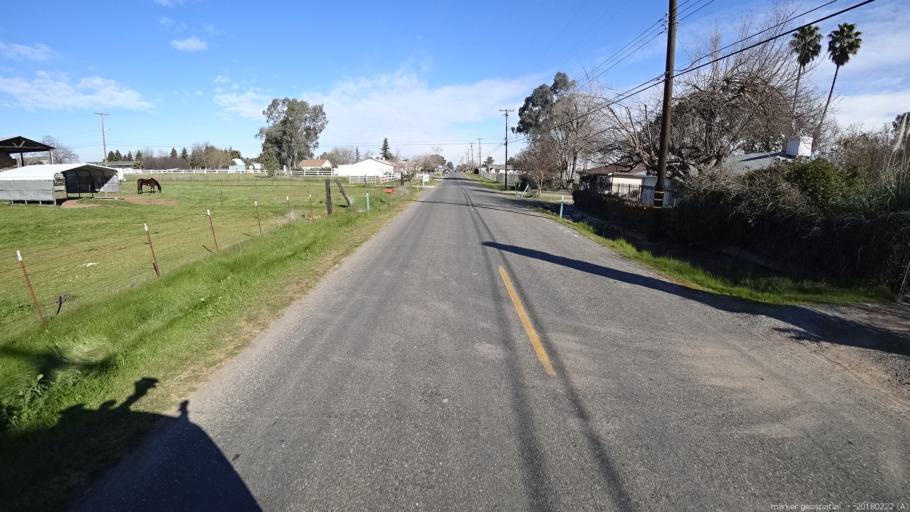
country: US
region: California
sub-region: Sacramento County
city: Elverta
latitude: 38.7235
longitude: -121.4575
